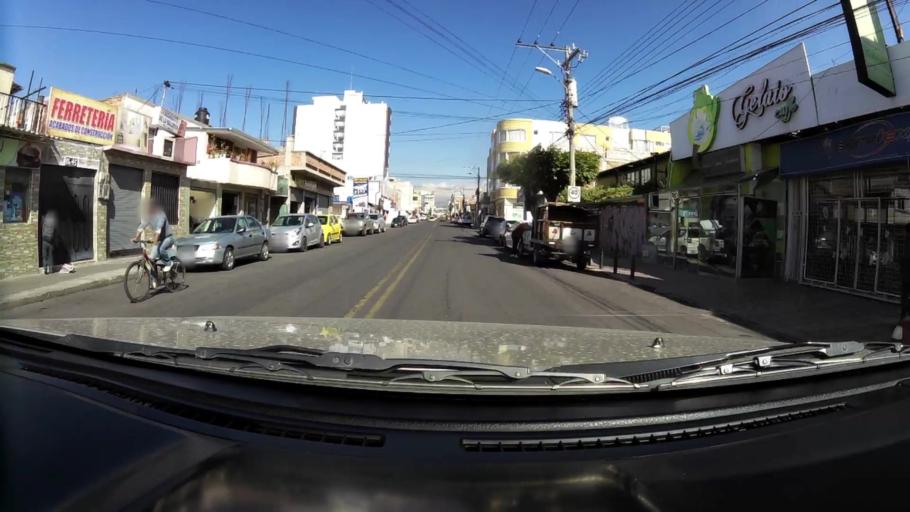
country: EC
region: Chimborazo
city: Riobamba
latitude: -1.6657
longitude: -78.6558
